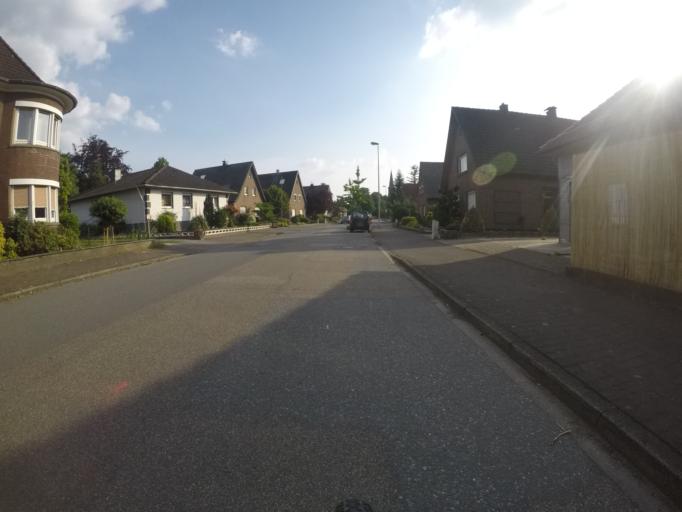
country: DE
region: North Rhine-Westphalia
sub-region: Regierungsbezirk Munster
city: Isselburg
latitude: 51.8359
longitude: 6.4664
